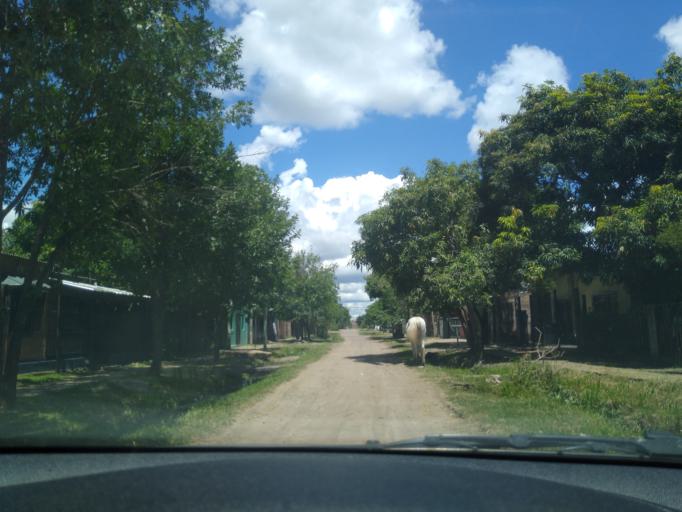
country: AR
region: Chaco
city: Barranqueras
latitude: -27.4698
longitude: -58.9333
